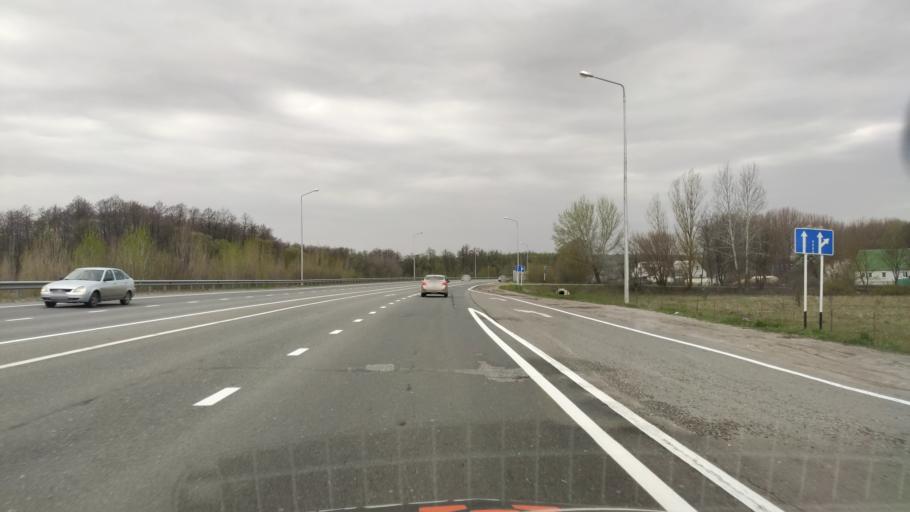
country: RU
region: Belgorod
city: Staryy Oskol
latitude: 51.3481
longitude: 37.8244
